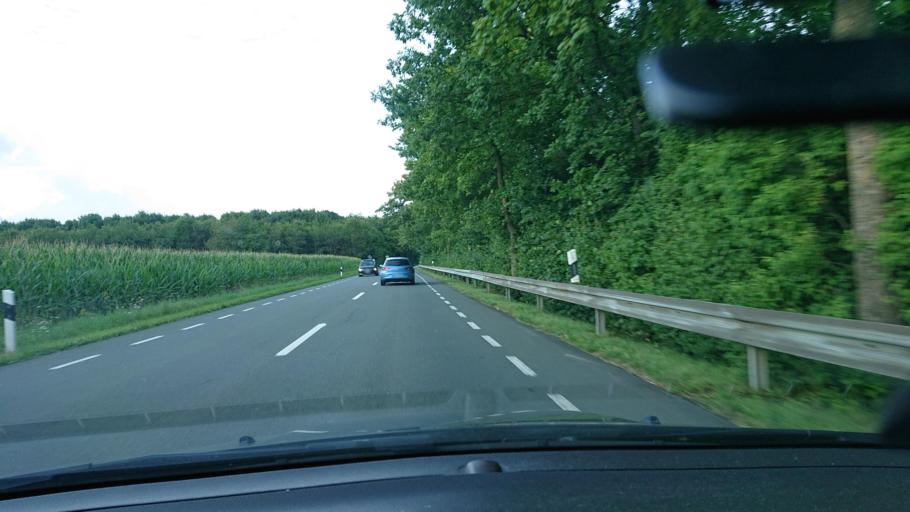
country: DE
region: North Rhine-Westphalia
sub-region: Regierungsbezirk Arnsberg
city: Mohnesee
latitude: 51.5012
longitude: 8.0602
